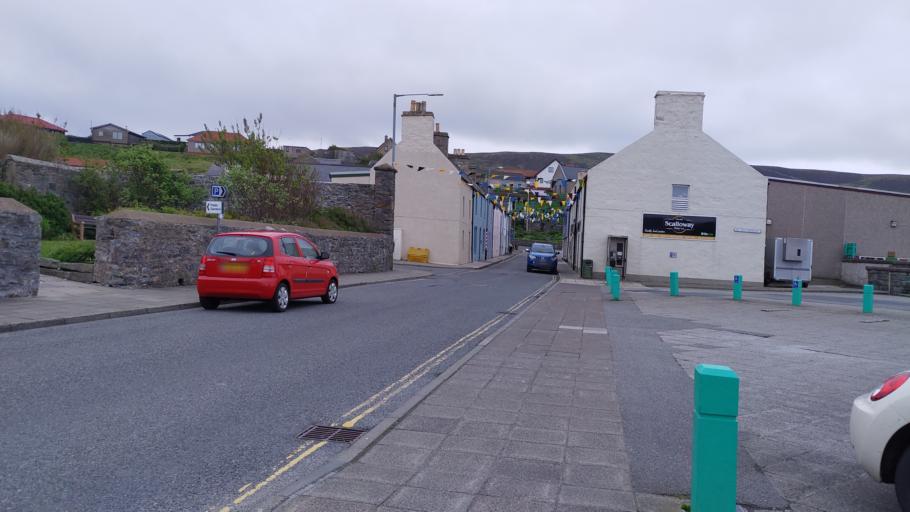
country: GB
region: Scotland
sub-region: Shetland Islands
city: Lerwick
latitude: 60.1374
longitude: -1.2772
